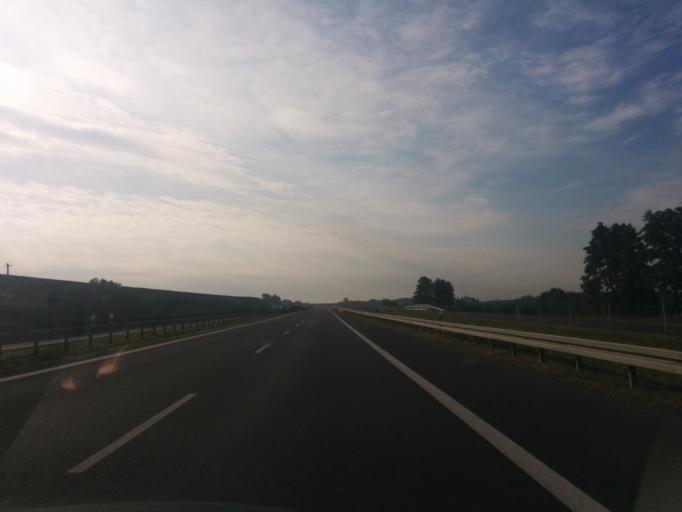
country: PL
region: Masovian Voivodeship
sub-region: Powiat grojecki
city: Jasieniec
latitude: 51.8089
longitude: 20.8861
